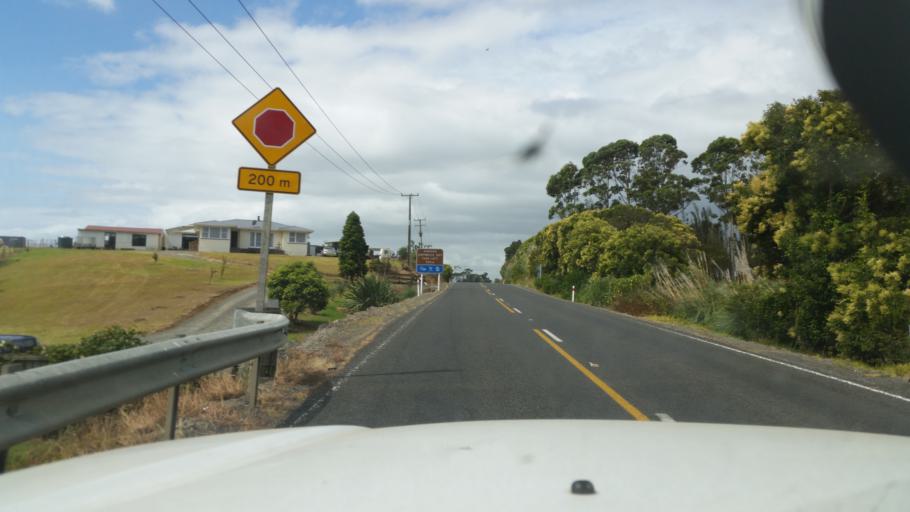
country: NZ
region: Northland
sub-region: Far North District
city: Ahipara
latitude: -35.1740
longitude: 173.1786
